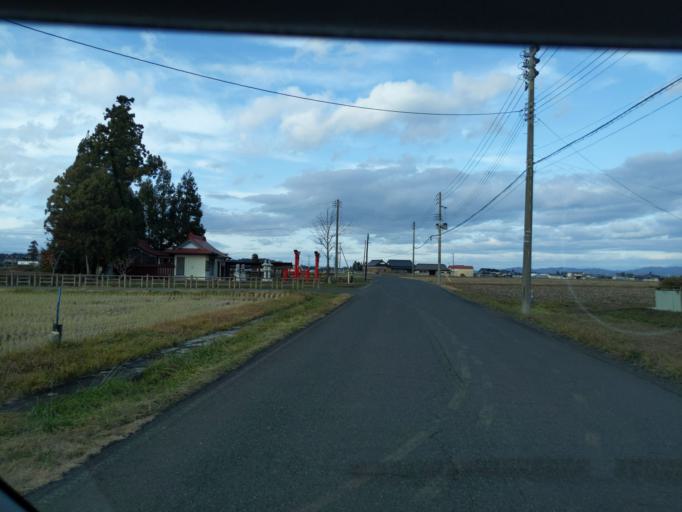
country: JP
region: Iwate
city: Mizusawa
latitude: 39.1494
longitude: 141.0894
